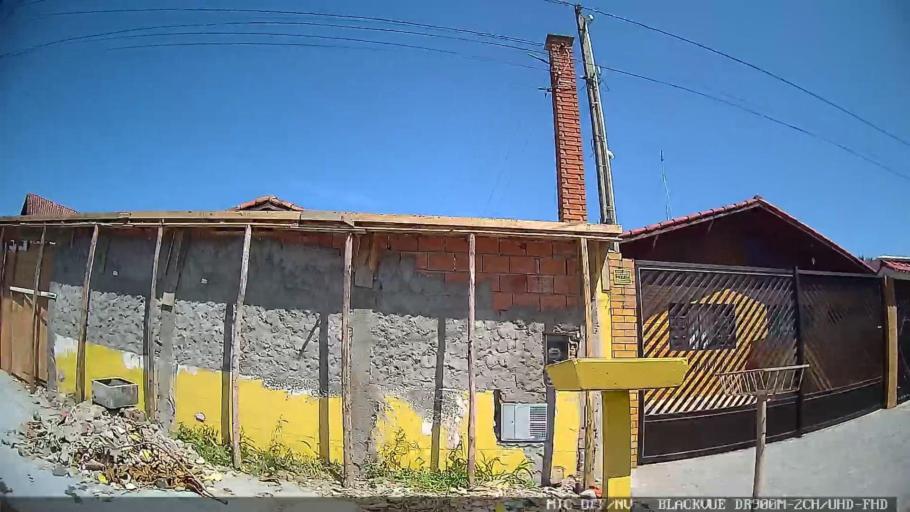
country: BR
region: Sao Paulo
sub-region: Peruibe
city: Peruibe
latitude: -24.3009
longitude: -46.9812
